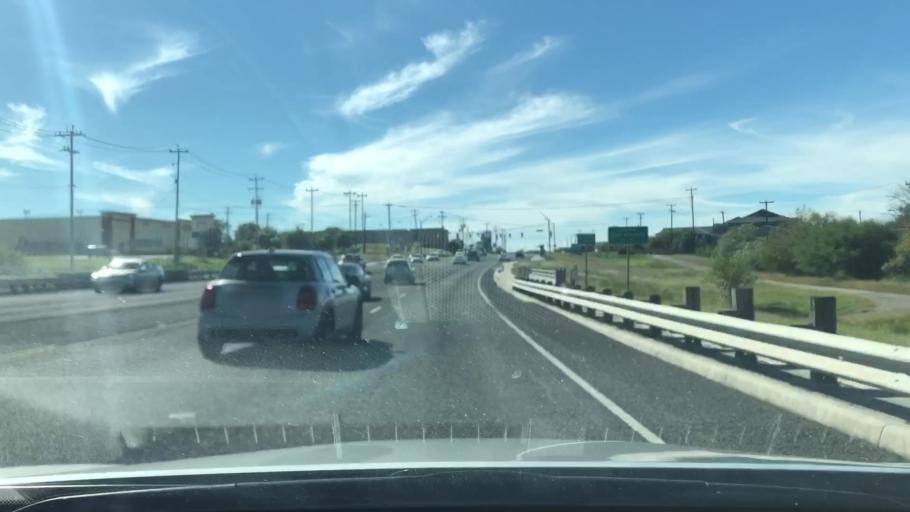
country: US
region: Texas
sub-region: Bexar County
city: Converse
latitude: 29.4862
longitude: -98.3450
